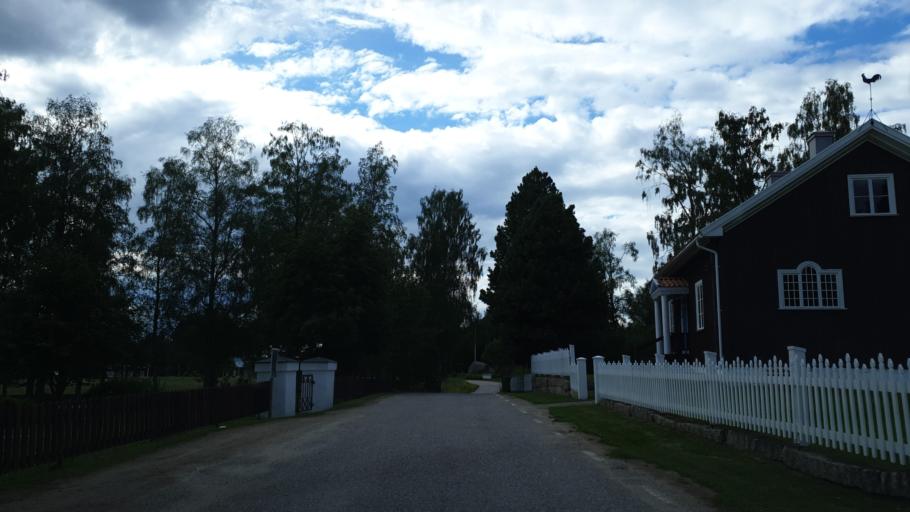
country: SE
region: Jaemtland
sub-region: Harjedalens Kommun
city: Sveg
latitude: 61.7980
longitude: 14.6438
